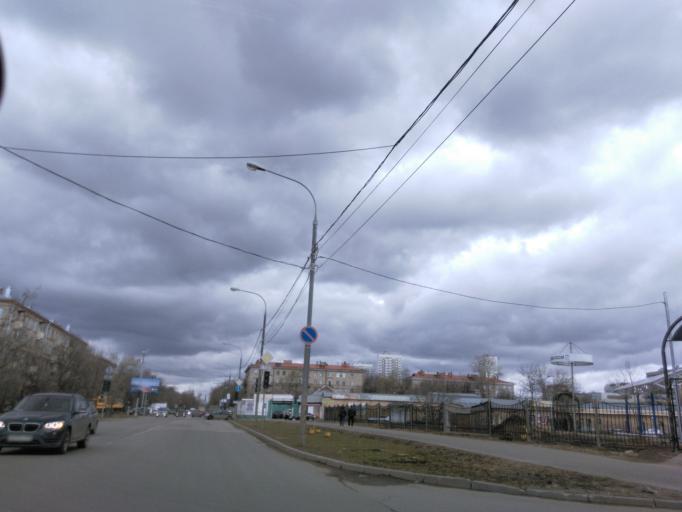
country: RU
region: Moskovskaya
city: Koptevo
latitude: 55.8324
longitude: 37.5199
